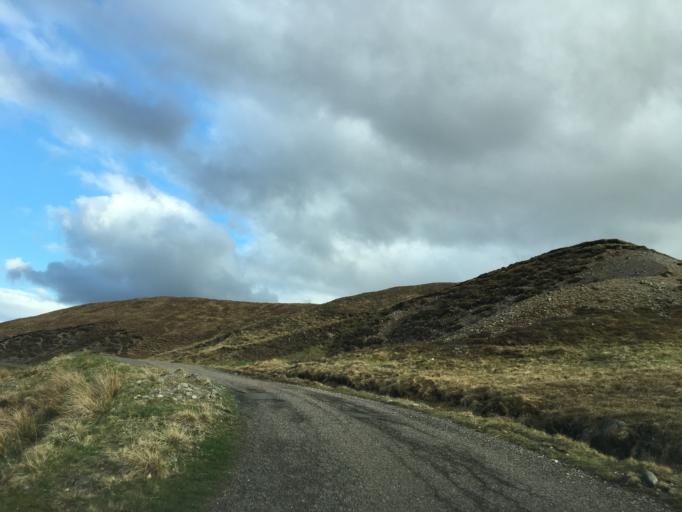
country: GB
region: Scotland
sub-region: Highland
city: Kingussie
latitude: 57.0118
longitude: -4.4194
